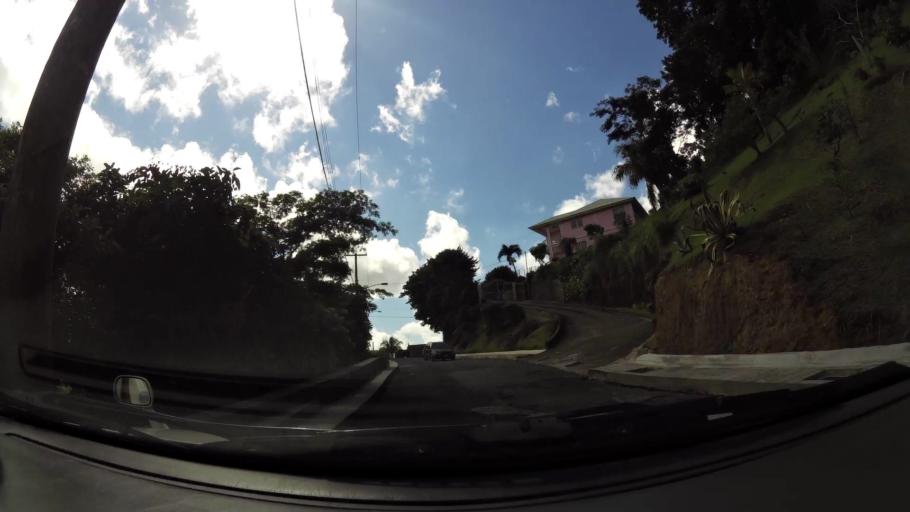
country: VC
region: Saint George
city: Kingstown
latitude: 13.1691
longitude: -61.2293
